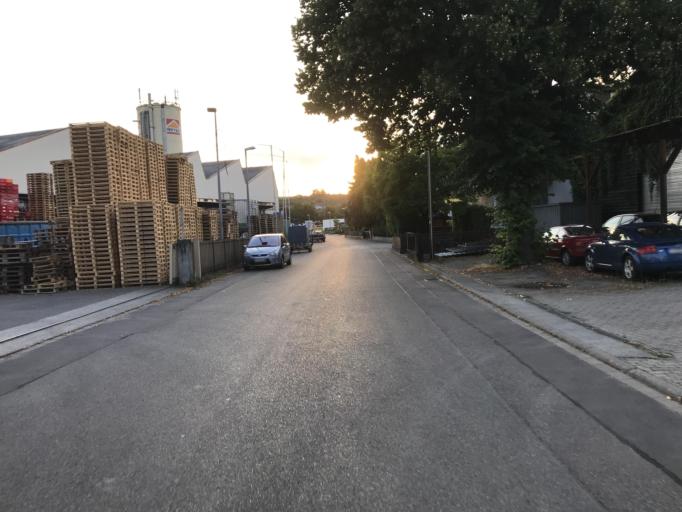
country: DE
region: Baden-Wuerttemberg
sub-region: Regierungsbezirk Stuttgart
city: Oberboihingen
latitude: 48.6450
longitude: 9.3618
